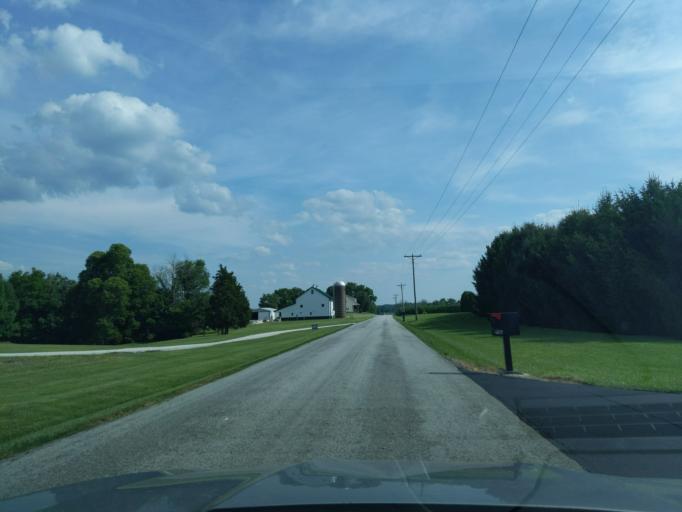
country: US
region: Indiana
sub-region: Decatur County
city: Greensburg
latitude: 39.2705
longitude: -85.4651
